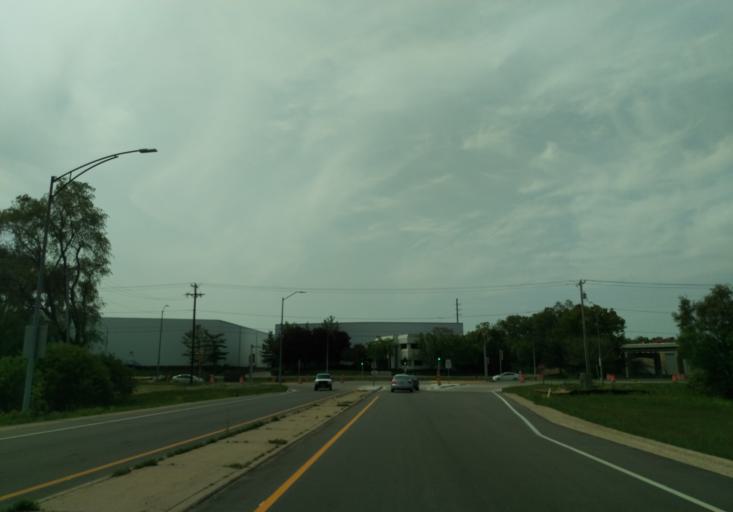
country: US
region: Wisconsin
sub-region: Dane County
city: Monona
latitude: 43.0849
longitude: -89.3100
